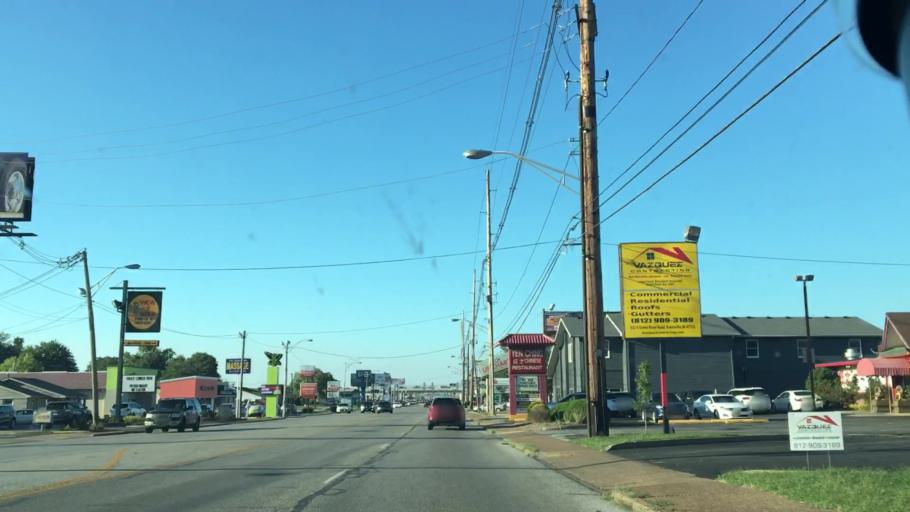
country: US
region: Indiana
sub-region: Vanderburgh County
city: Melody Hill
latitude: 37.9722
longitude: -87.4925
